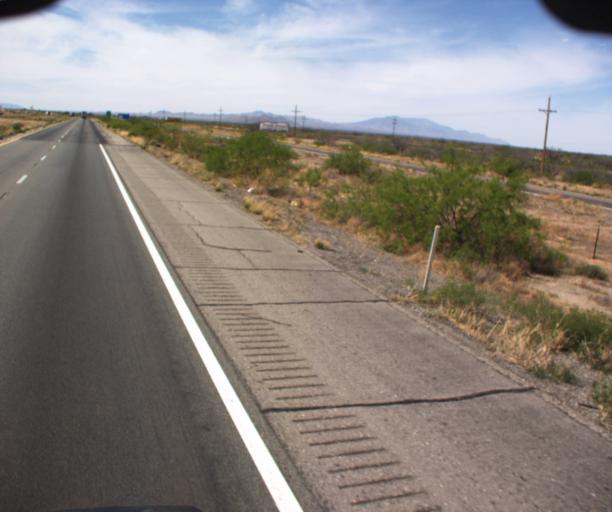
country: US
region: Arizona
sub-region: Cochise County
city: Willcox
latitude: 32.3160
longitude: -109.4349
